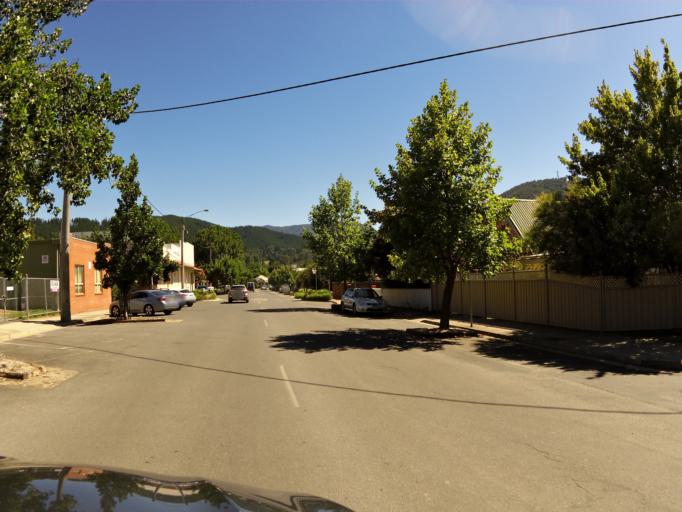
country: AU
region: Victoria
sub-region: Alpine
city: Mount Beauty
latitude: -36.7297
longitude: 146.9620
